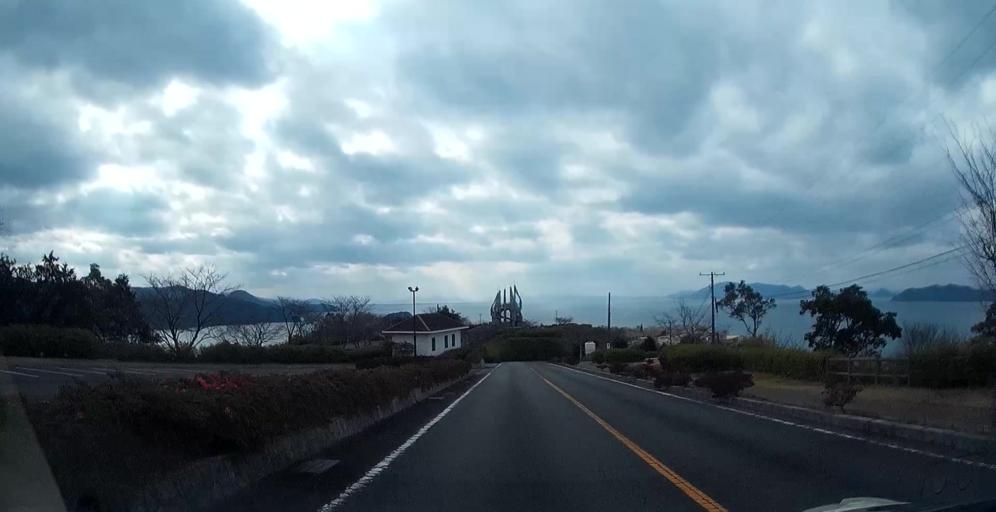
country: JP
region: Kumamoto
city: Yatsushiro
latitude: 32.3686
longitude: 130.4975
